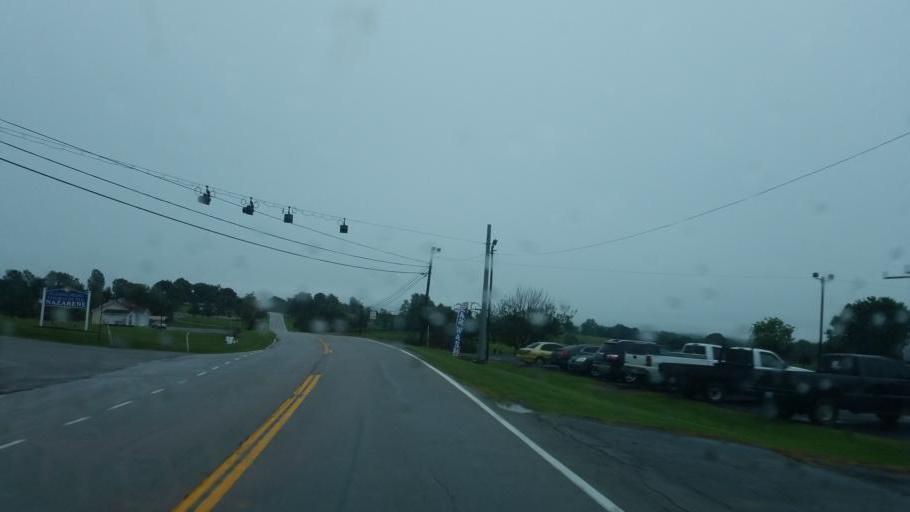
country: US
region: Kentucky
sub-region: Fleming County
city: Flemingsburg
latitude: 38.3926
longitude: -83.6908
